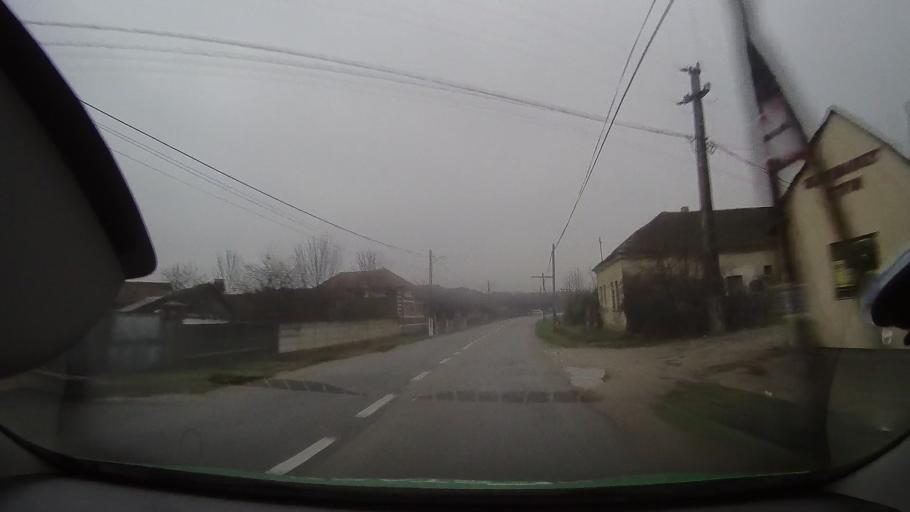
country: RO
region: Bihor
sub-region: Comuna Tinca
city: Gurbediu
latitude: 46.7896
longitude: 21.8665
